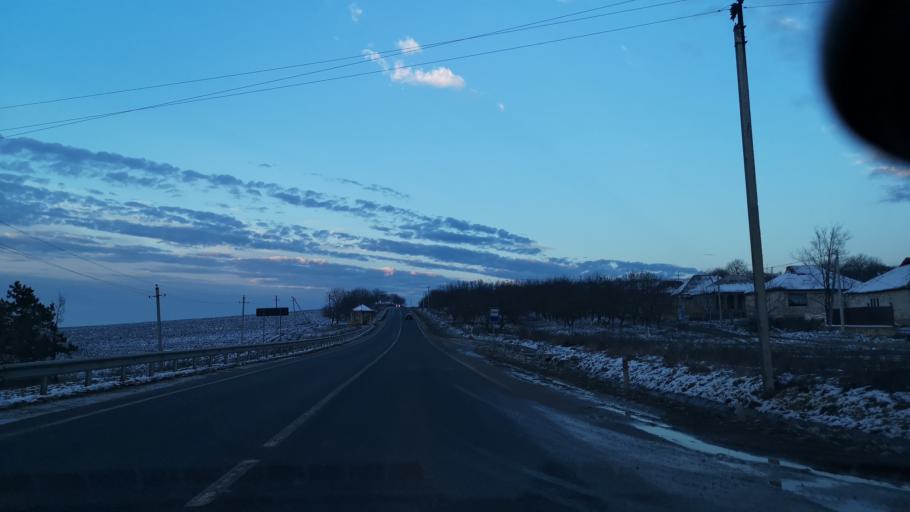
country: MD
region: Rezina
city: Saharna
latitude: 47.5912
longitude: 28.8218
